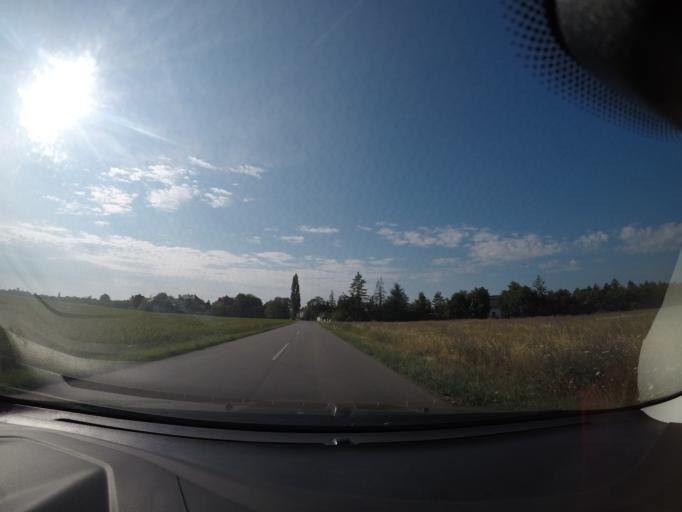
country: AT
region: Lower Austria
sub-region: Politischer Bezirk Baden
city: Tattendorf
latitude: 47.9305
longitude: 16.2987
